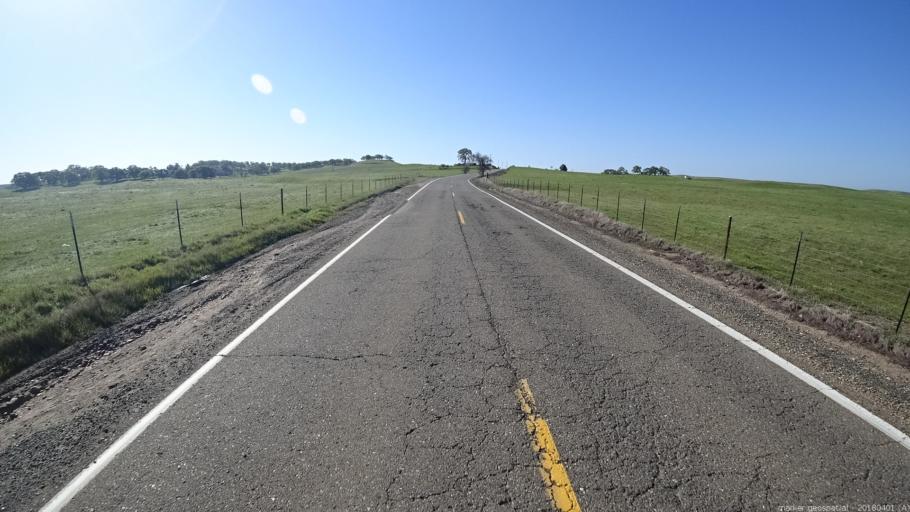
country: US
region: California
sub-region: Sacramento County
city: Rancho Murieta
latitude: 38.4671
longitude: -121.0438
